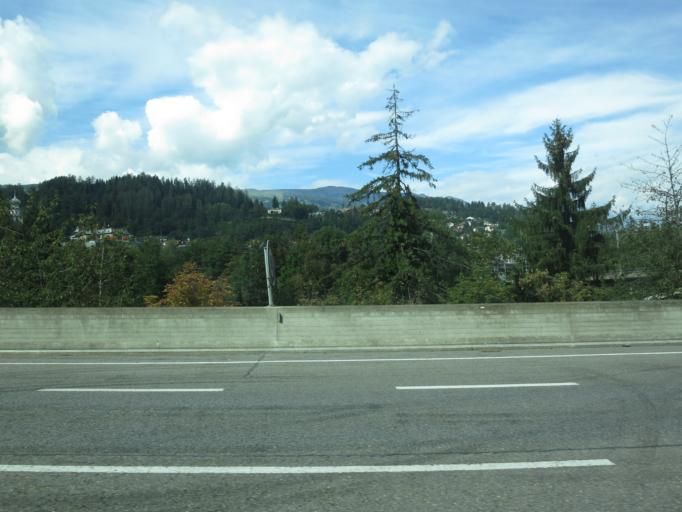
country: CH
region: Grisons
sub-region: Hinterrhein District
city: Thusis
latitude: 46.6939
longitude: 9.4434
